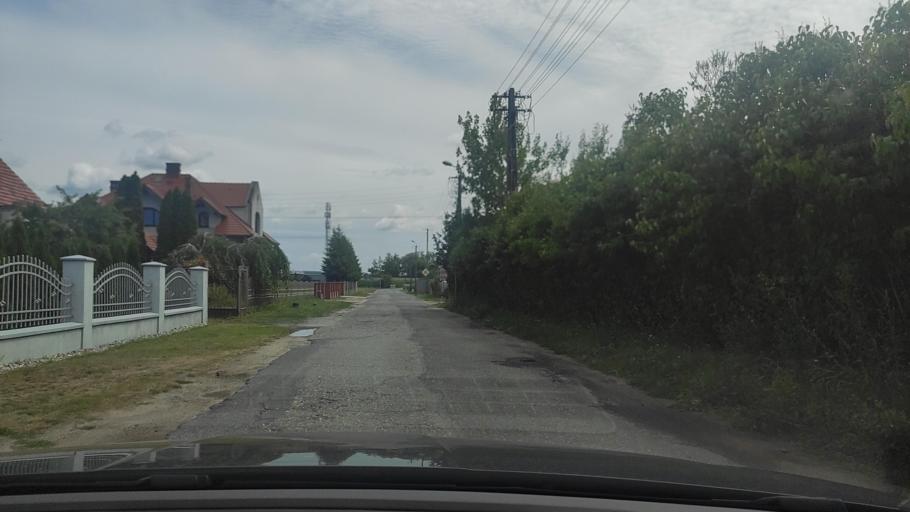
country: PL
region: Greater Poland Voivodeship
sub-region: Powiat poznanski
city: Kostrzyn
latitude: 52.4026
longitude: 17.2112
